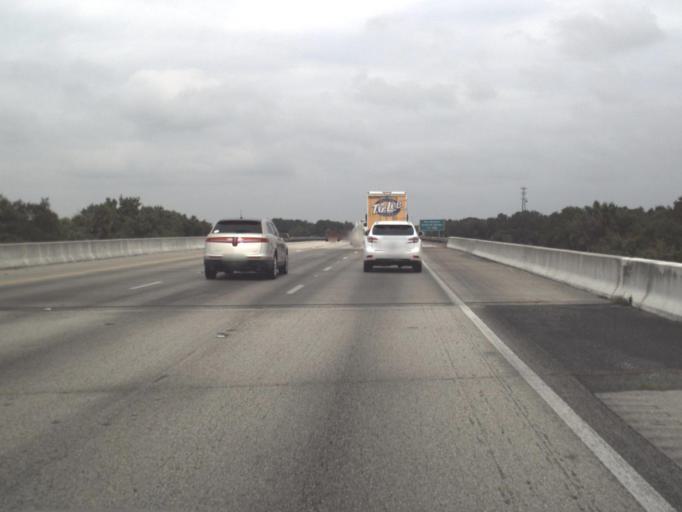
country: US
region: Florida
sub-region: Manatee County
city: Ellenton
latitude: 27.5562
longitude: -82.5112
